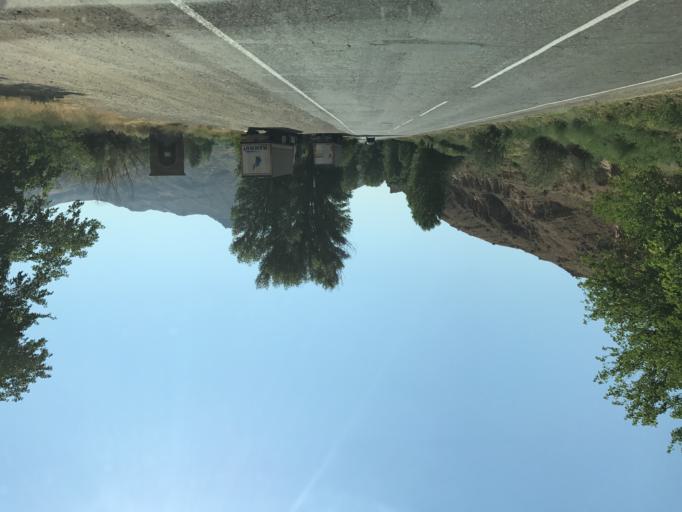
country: AM
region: Vayots' Dzori Marz
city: Getap'
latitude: 39.7362
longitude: 45.2898
